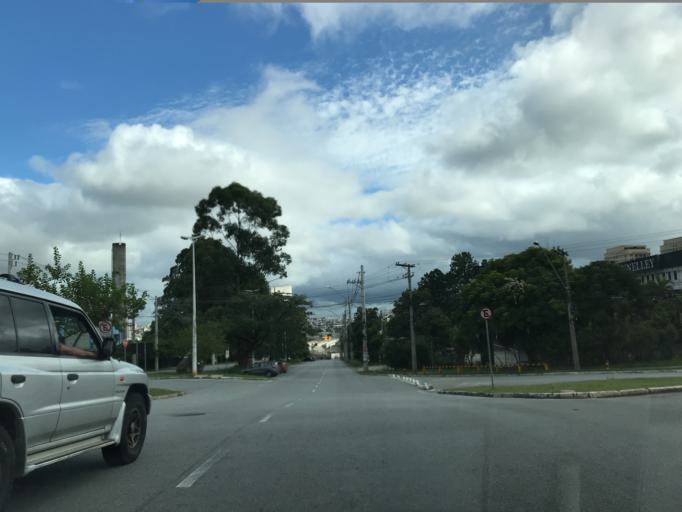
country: BR
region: Sao Paulo
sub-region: Carapicuiba
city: Carapicuiba
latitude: -23.4978
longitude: -46.8367
